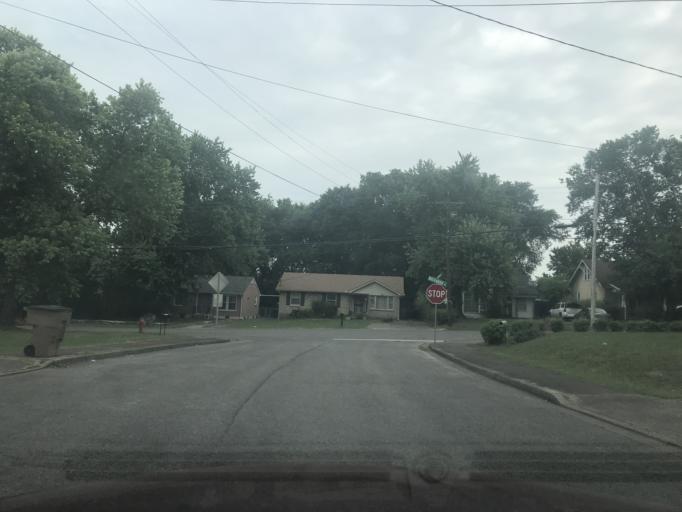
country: US
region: Tennessee
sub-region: Davidson County
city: Nashville
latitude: 36.1801
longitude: -86.8204
